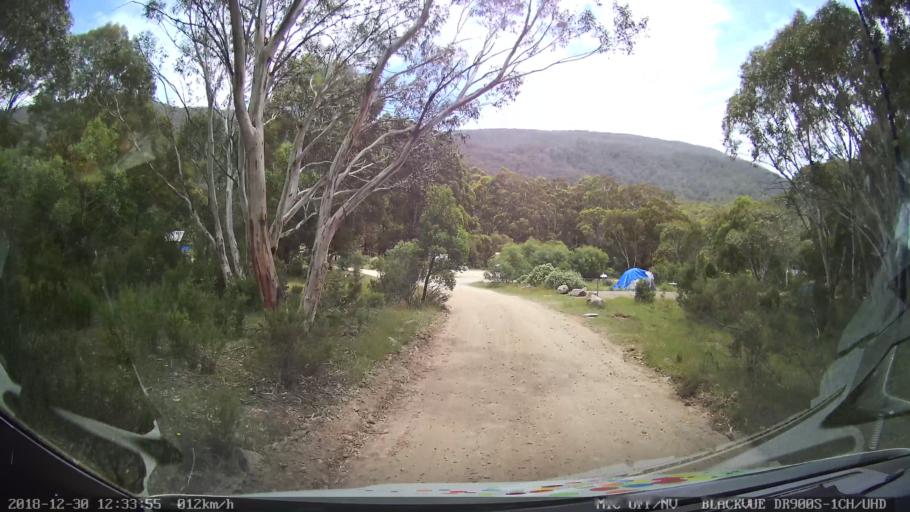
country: AU
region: New South Wales
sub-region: Snowy River
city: Jindabyne
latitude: -36.3225
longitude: 148.4666
